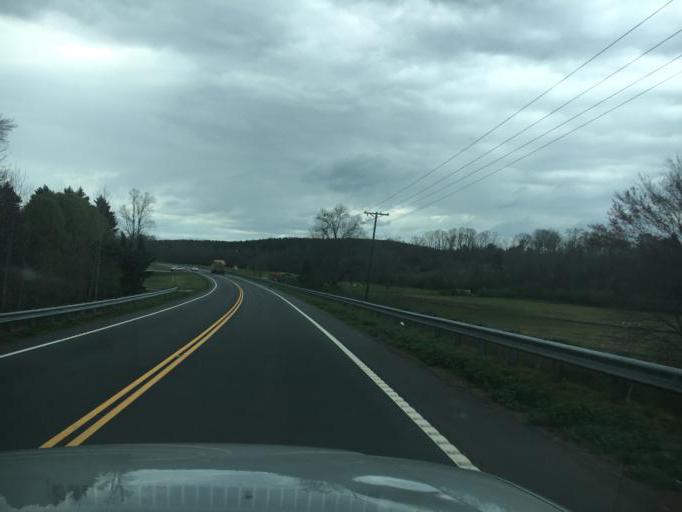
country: US
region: South Carolina
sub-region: Oconee County
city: Walhalla
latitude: 34.7841
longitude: -83.0191
